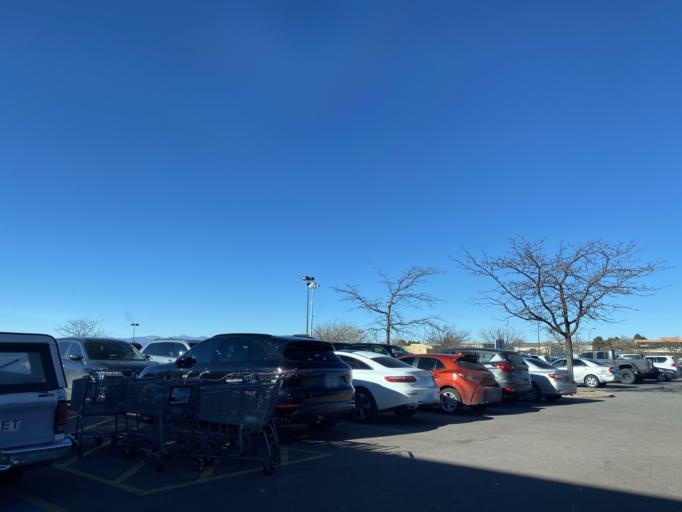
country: US
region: New Mexico
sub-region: Santa Fe County
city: Santa Fe
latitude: 35.6579
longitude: -105.9596
